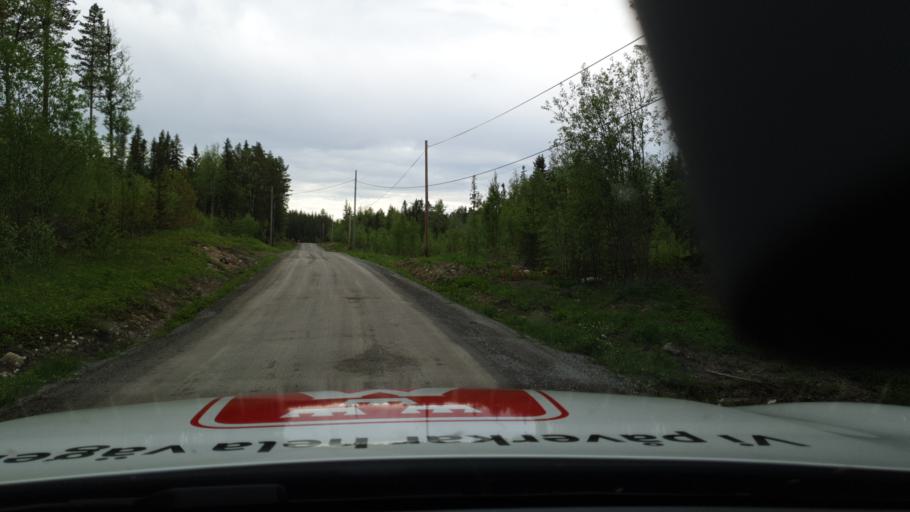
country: SE
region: Jaemtland
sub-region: OEstersunds Kommun
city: Brunflo
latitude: 62.9876
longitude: 14.7136
